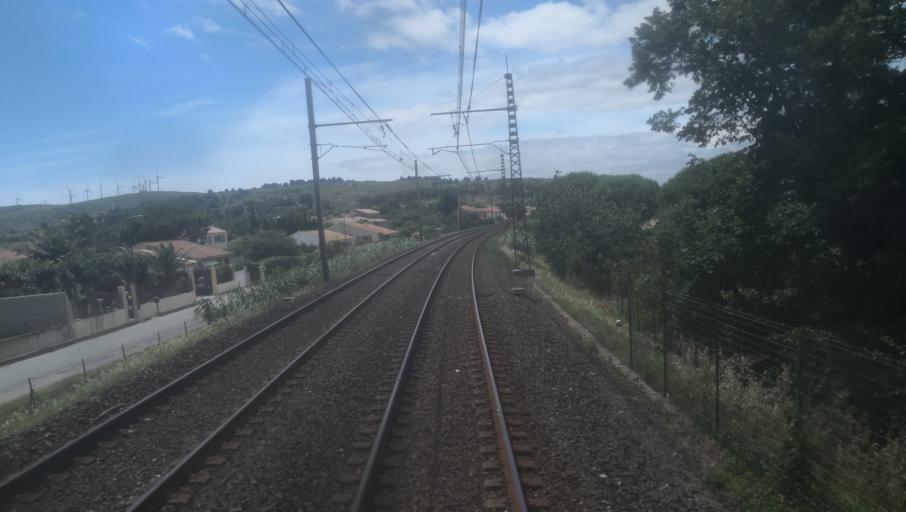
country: FR
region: Languedoc-Roussillon
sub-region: Departement de l'Aude
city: Nevian
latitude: 43.2099
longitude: 2.9029
